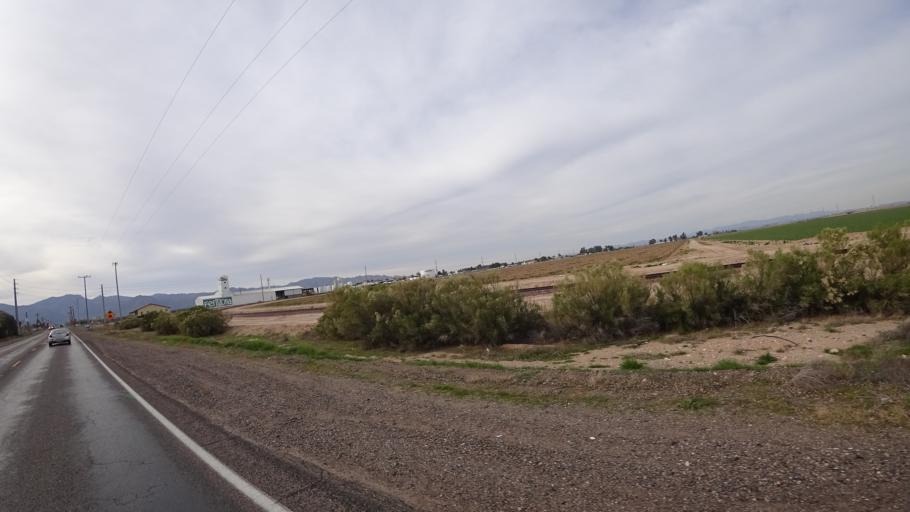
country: US
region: Arizona
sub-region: Maricopa County
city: Citrus Park
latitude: 33.5662
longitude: -112.4245
